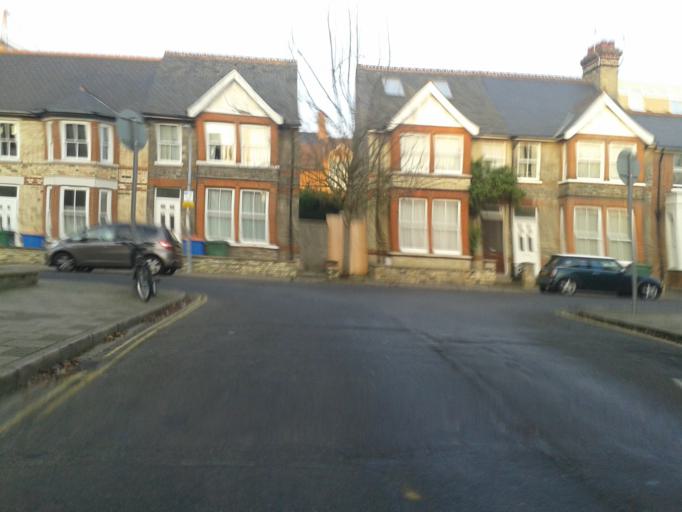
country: GB
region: England
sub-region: Cambridgeshire
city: Cambridge
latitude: 52.2020
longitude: 0.1347
